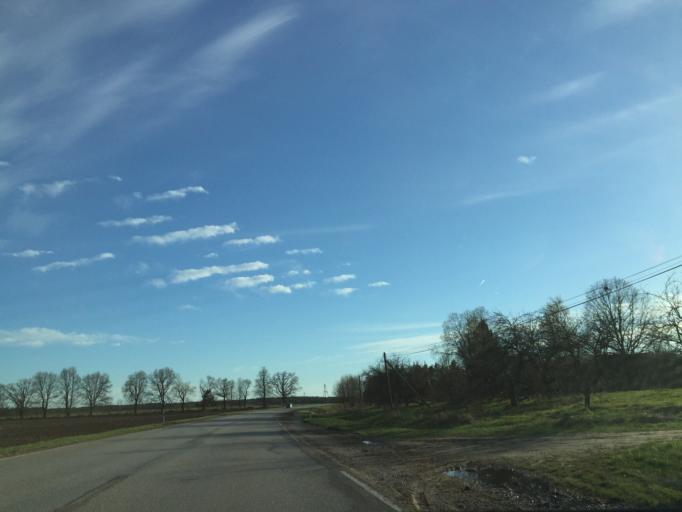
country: LV
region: Valkas Rajons
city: Valka
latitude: 57.7488
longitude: 25.9630
